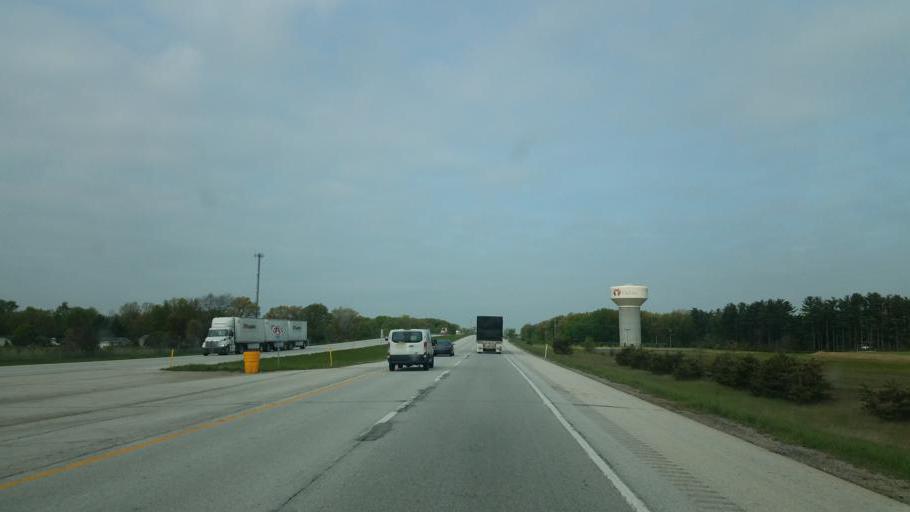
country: US
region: Indiana
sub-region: Elkhart County
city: Bristol
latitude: 41.7301
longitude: -85.8924
